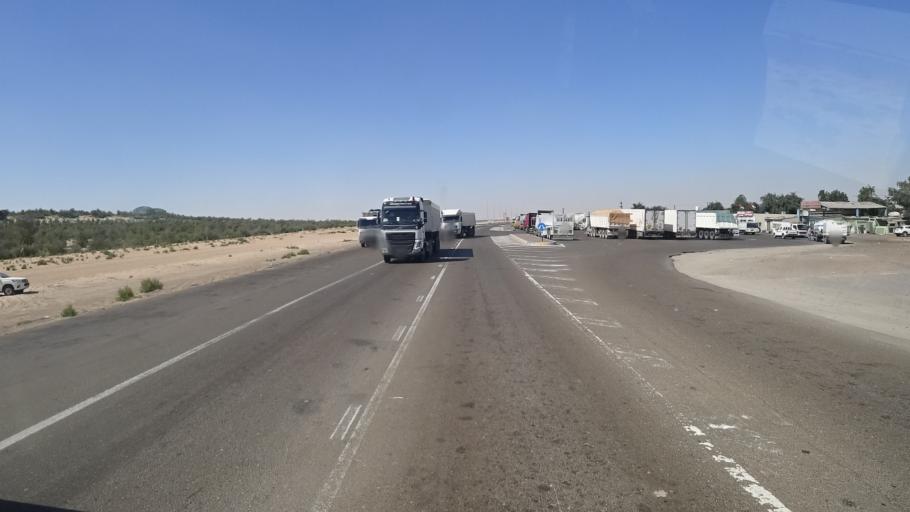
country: AE
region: Abu Dhabi
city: Al Ain
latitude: 24.1331
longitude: 55.0887
